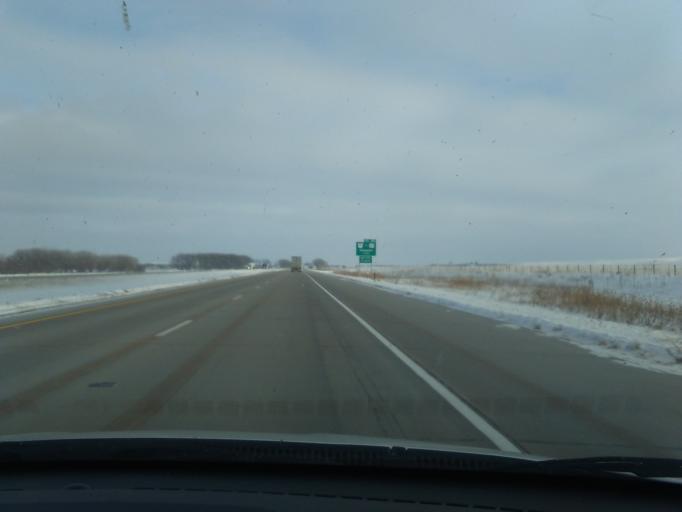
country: US
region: Nebraska
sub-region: Deuel County
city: Chappell
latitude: 41.0868
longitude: -102.4985
